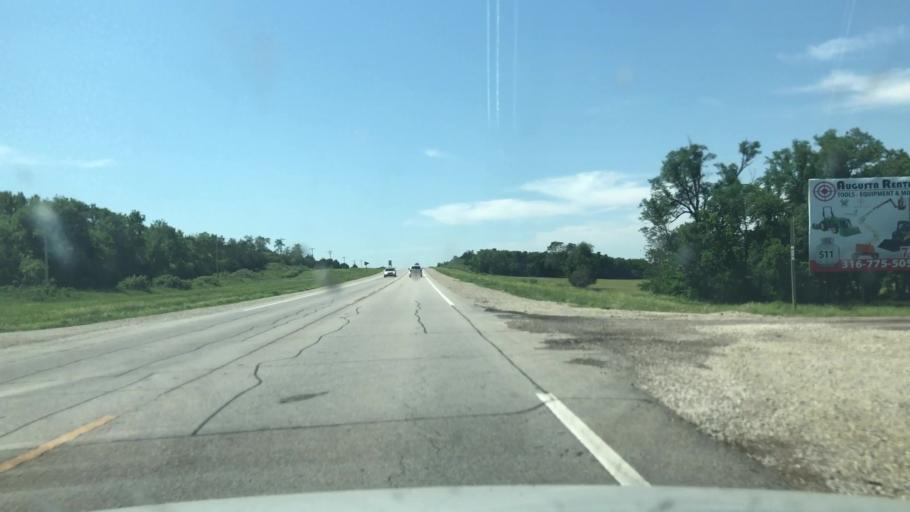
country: US
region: Kansas
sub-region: Cowley County
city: Winfield
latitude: 37.3757
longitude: -97.0071
